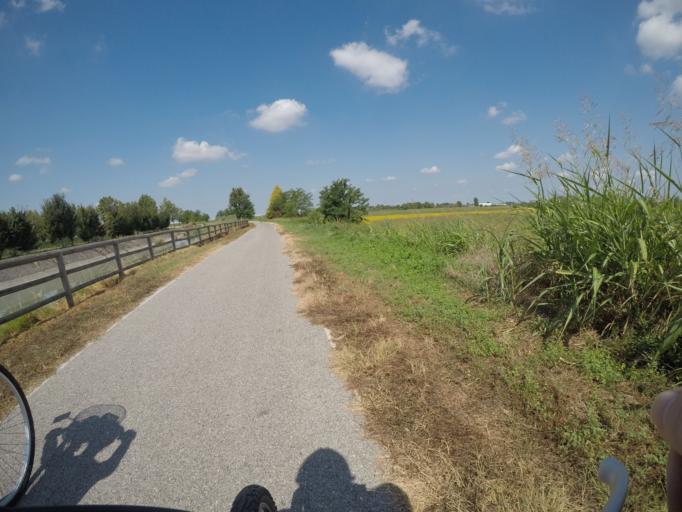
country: IT
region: Veneto
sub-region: Provincia di Rovigo
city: Villanova del Ghebbo Canton
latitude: 45.0649
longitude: 11.6218
